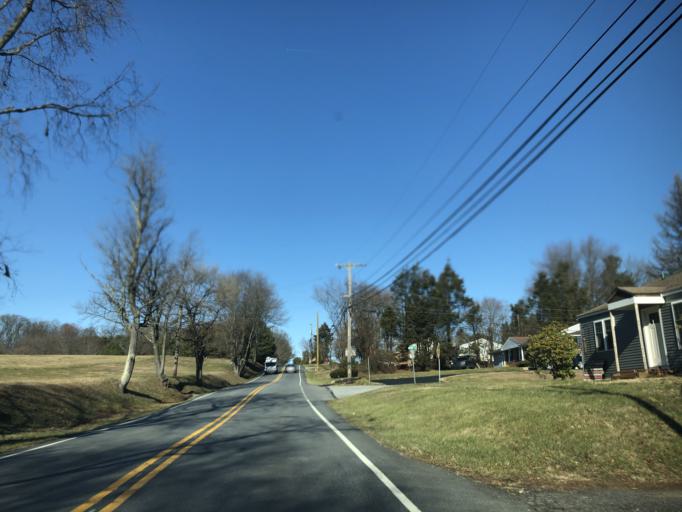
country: US
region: Pennsylvania
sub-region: Chester County
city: South Coatesville
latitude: 39.9392
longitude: -75.8326
